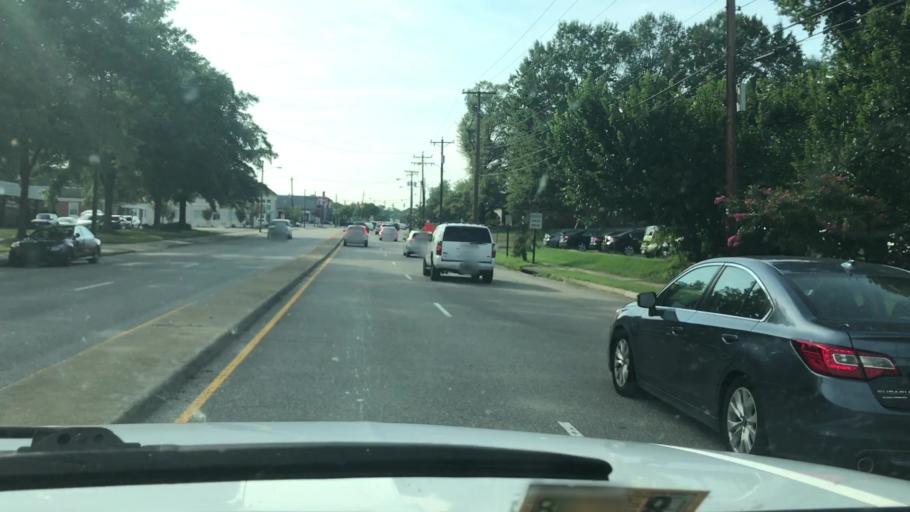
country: US
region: Virginia
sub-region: Henrico County
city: Dumbarton
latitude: 37.5768
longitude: -77.5102
